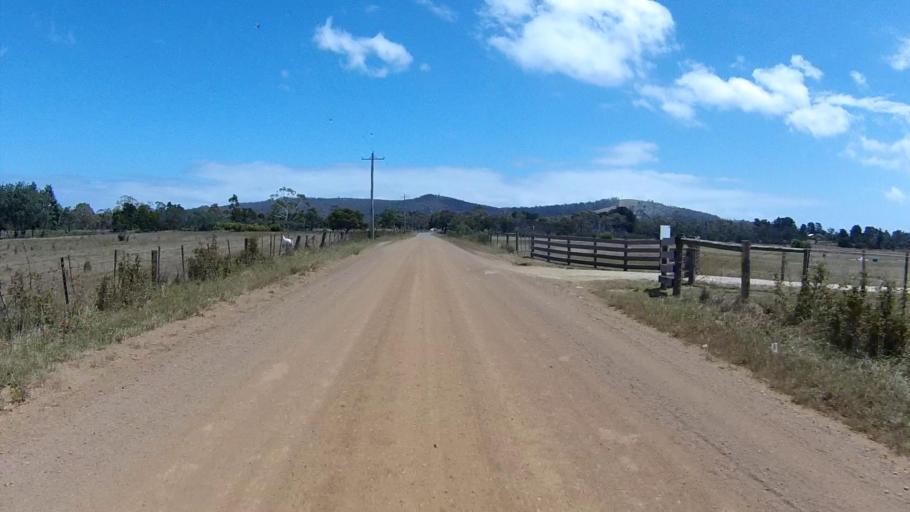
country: AU
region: Tasmania
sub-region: Clarence
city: Sandford
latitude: -42.9345
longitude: 147.5064
